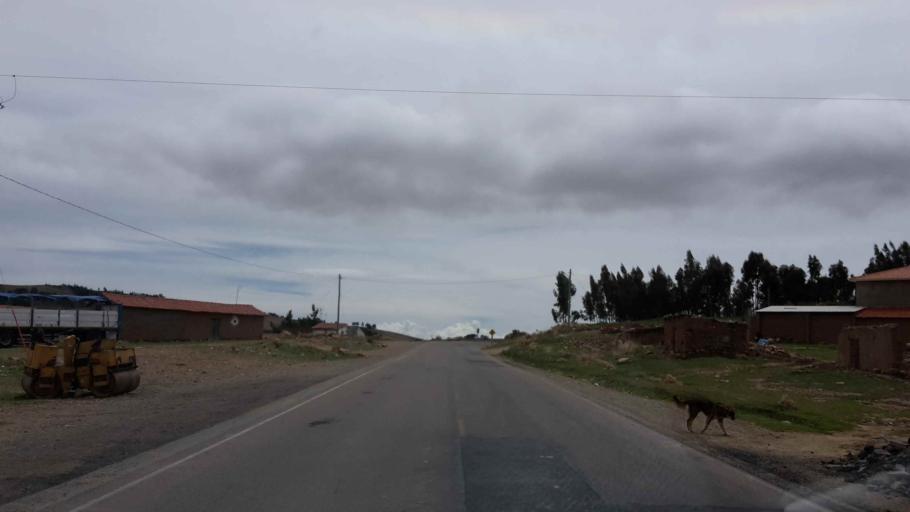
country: BO
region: Cochabamba
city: Arani
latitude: -17.4775
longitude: -65.6329
